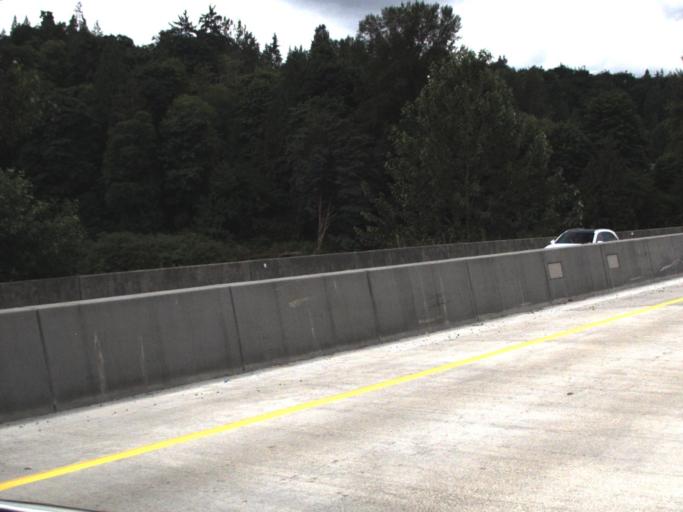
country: US
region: Washington
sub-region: Snohomish County
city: Cathcart
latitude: 47.8315
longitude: -122.0468
